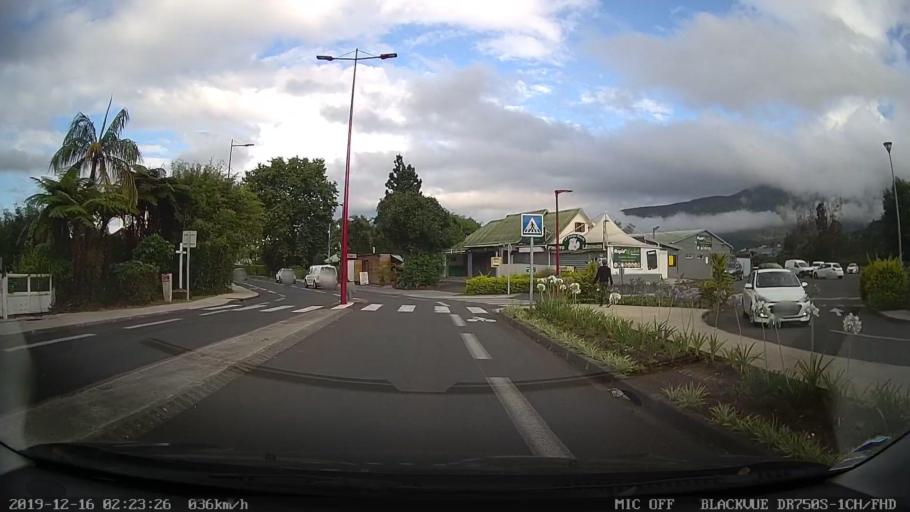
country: RE
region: Reunion
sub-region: Reunion
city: Salazie
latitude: -21.1428
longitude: 55.6210
